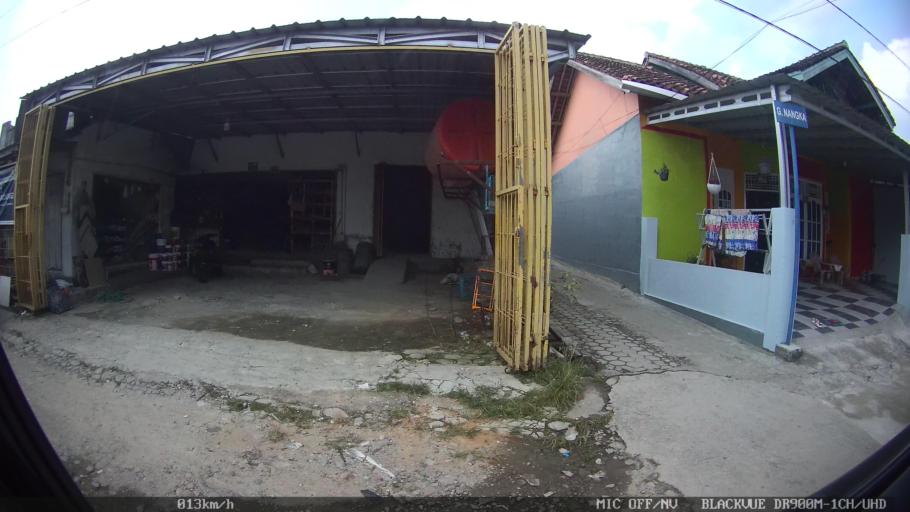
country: ID
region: Lampung
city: Pringsewu
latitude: -5.3577
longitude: 104.9724
